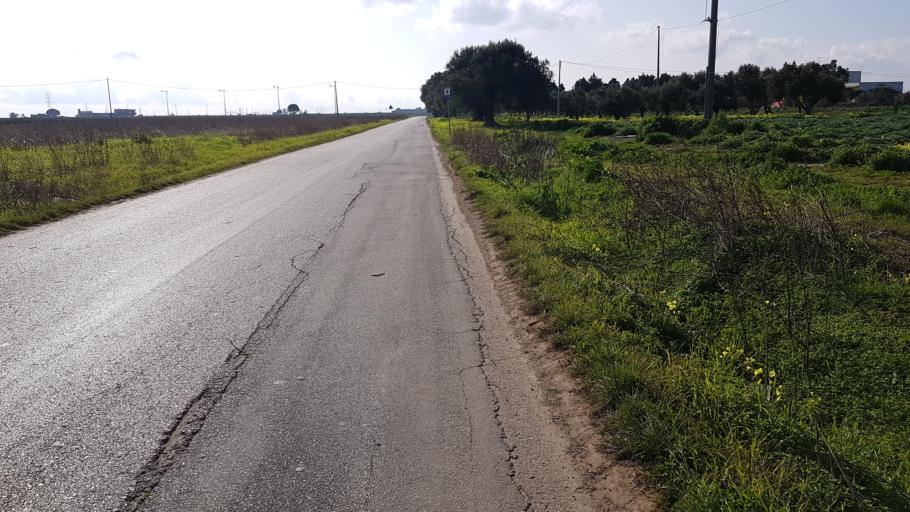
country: IT
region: Apulia
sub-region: Provincia di Brindisi
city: La Rosa
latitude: 40.5810
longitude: 17.9021
